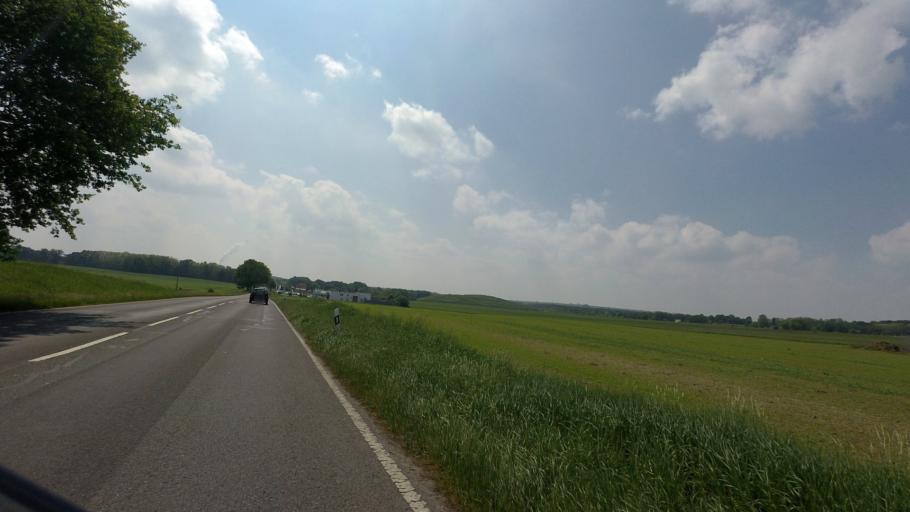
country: DE
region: Brandenburg
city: Spremberg
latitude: 51.5959
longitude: 14.3634
